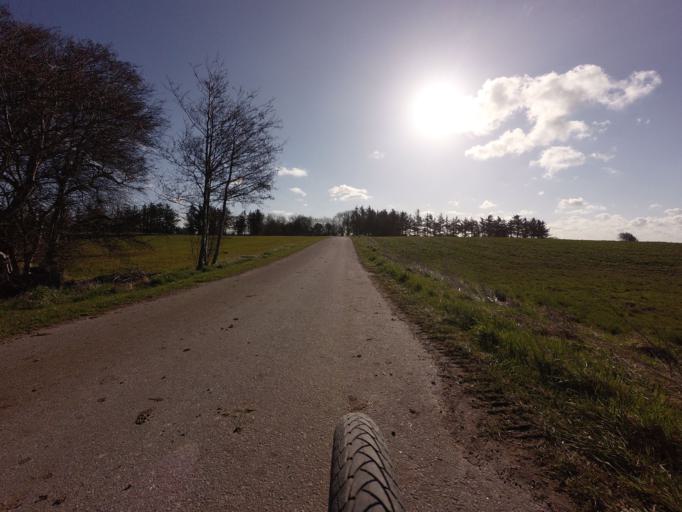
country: DK
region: North Denmark
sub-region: Hjorring Kommune
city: Vra
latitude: 57.3603
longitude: 9.8185
